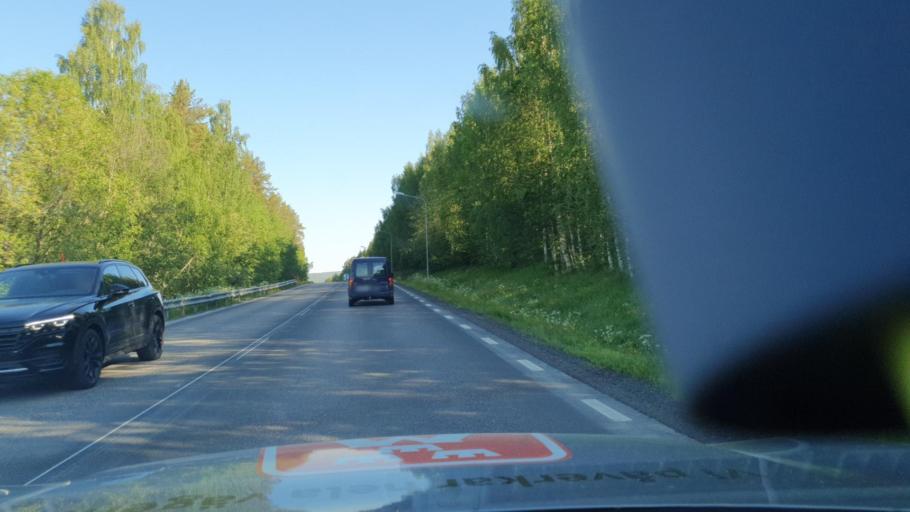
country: SE
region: Norrbotten
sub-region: Bodens Kommun
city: Boden
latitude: 65.8399
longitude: 21.6080
